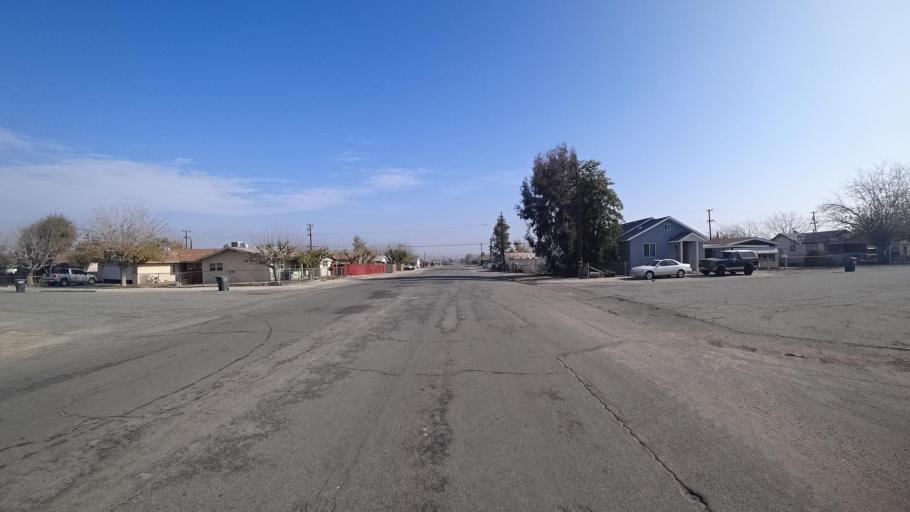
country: US
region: California
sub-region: Kern County
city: Ford City
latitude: 35.1576
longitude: -119.4591
